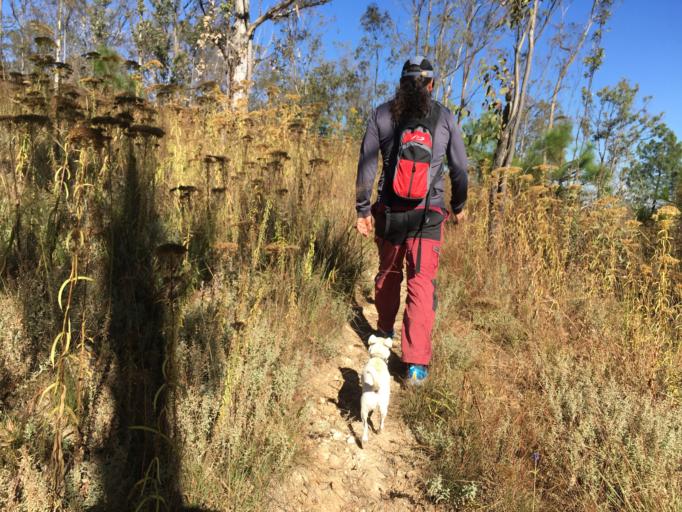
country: MX
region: Michoacan
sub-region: Morelia
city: Montana Monarca (Punta Altozano)
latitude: 19.6672
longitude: -101.1467
